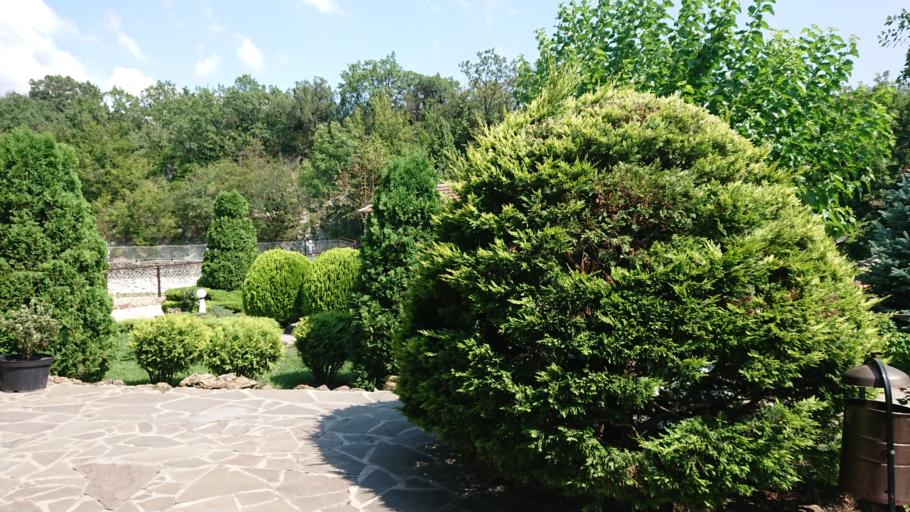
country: RU
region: Krasnodarskiy
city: Kabardinka
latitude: 44.6618
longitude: 37.9227
